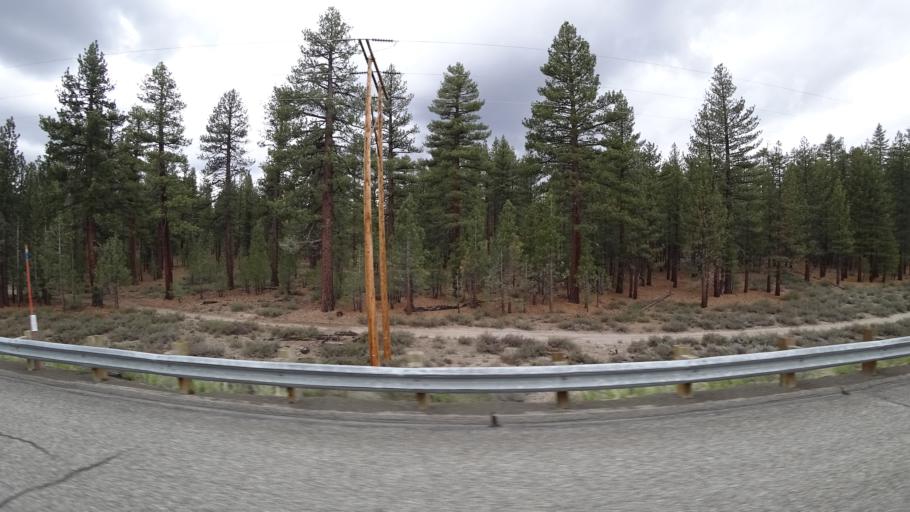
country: US
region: California
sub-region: Mono County
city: Mammoth Lakes
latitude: 37.7204
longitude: -118.9601
